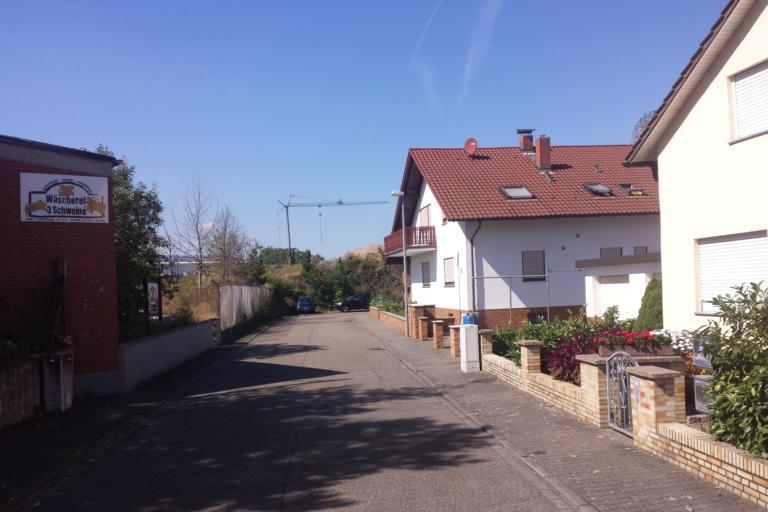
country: DE
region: Hesse
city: Viernheim
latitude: 49.5475
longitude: 8.5885
